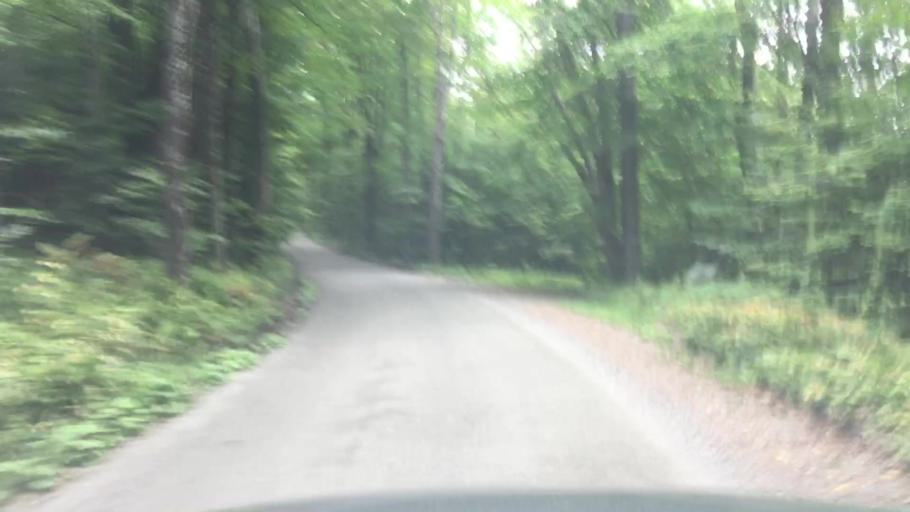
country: US
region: Vermont
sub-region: Windham County
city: Dover
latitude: 42.8472
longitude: -72.7721
